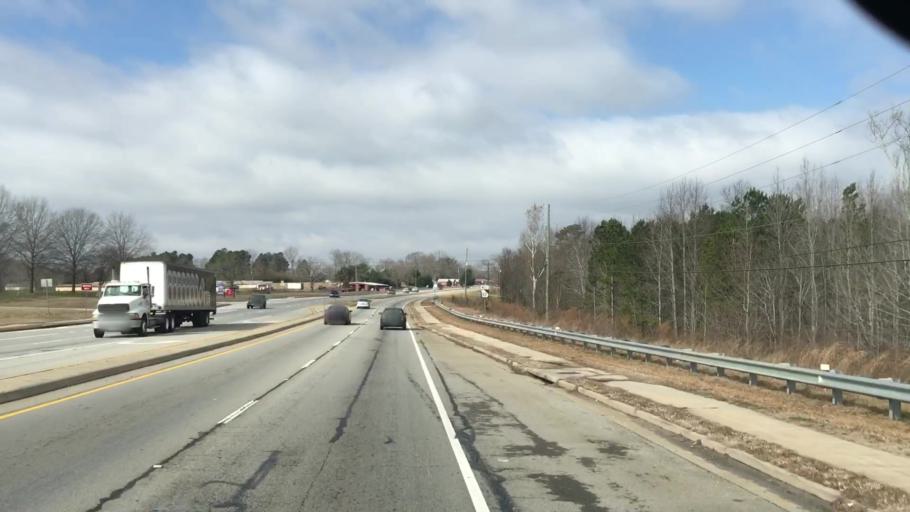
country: US
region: Georgia
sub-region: Hall County
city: Oakwood
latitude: 34.1681
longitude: -83.8336
